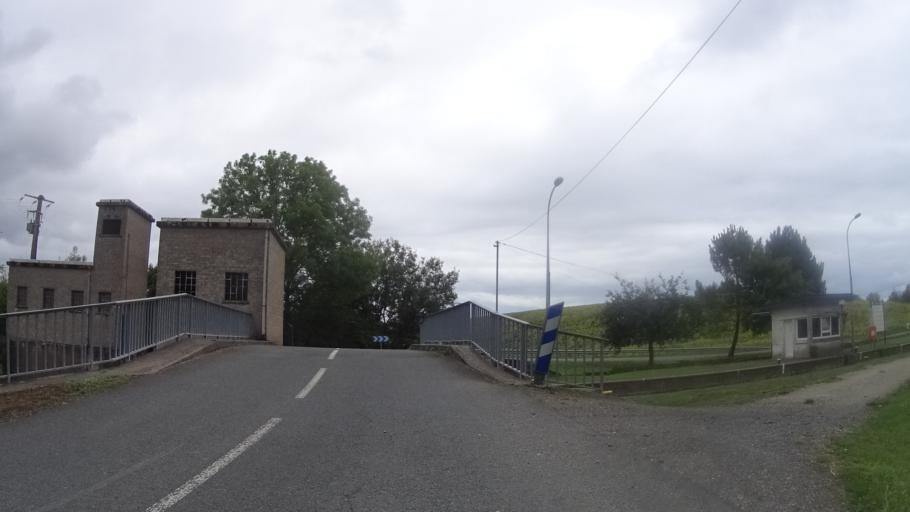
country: FR
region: Lorraine
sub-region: Departement de la Moselle
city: Dieuze
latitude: 48.6892
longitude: 6.6851
